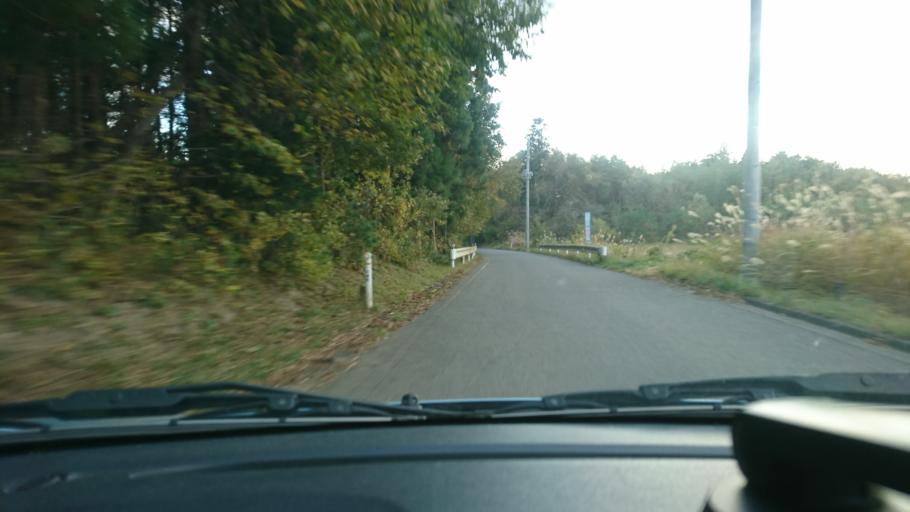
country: JP
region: Iwate
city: Ichinoseki
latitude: 38.7817
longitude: 141.2166
